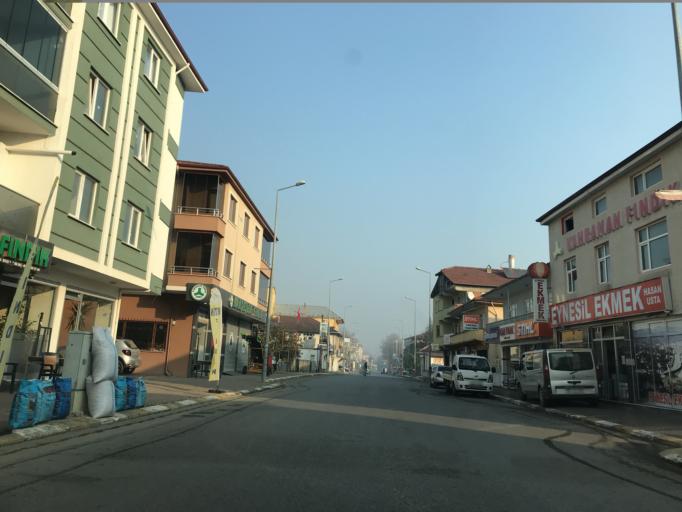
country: TR
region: Duzce
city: Cumayeri
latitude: 40.8775
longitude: 30.9503
